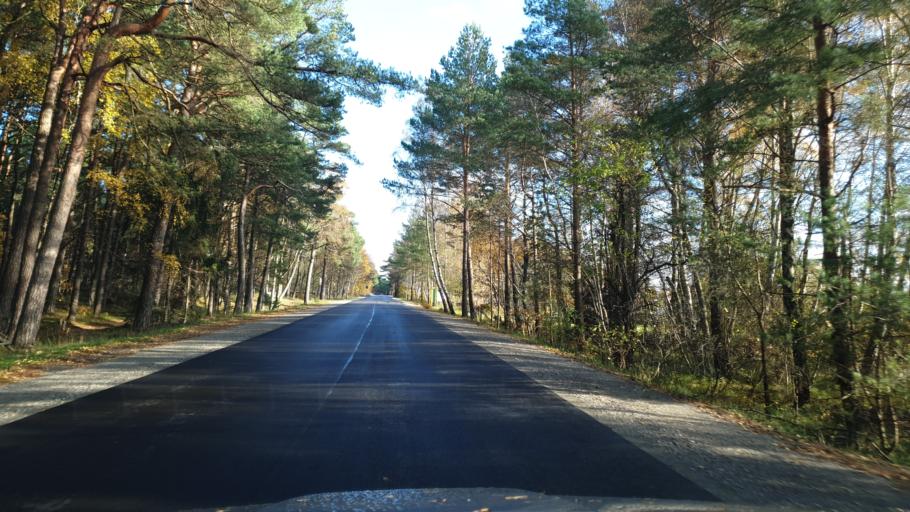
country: PL
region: Pomeranian Voivodeship
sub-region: Powiat pucki
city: Jastrzebia Gora
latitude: 54.8307
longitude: 18.2299
